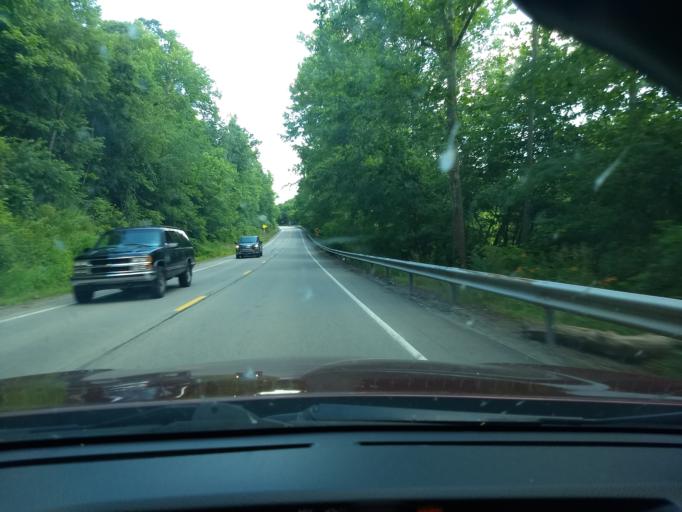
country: US
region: Pennsylvania
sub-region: Westmoreland County
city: Irwin
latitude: 40.3525
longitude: -79.7327
